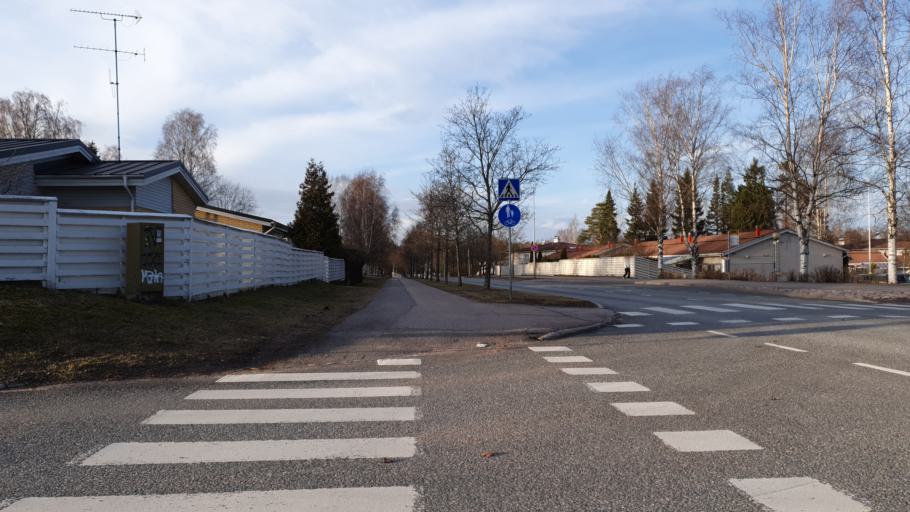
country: FI
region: Uusimaa
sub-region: Helsinki
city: Vantaa
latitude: 60.3194
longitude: 25.0137
